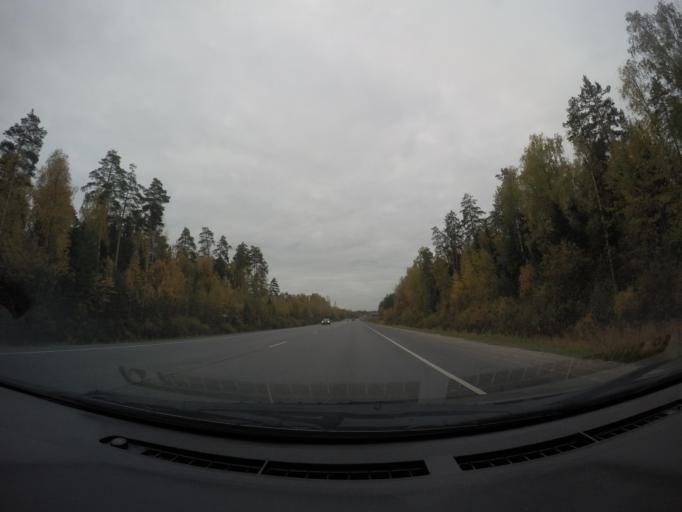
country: RU
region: Moskovskaya
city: Fryazevo
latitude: 55.7043
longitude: 38.4323
